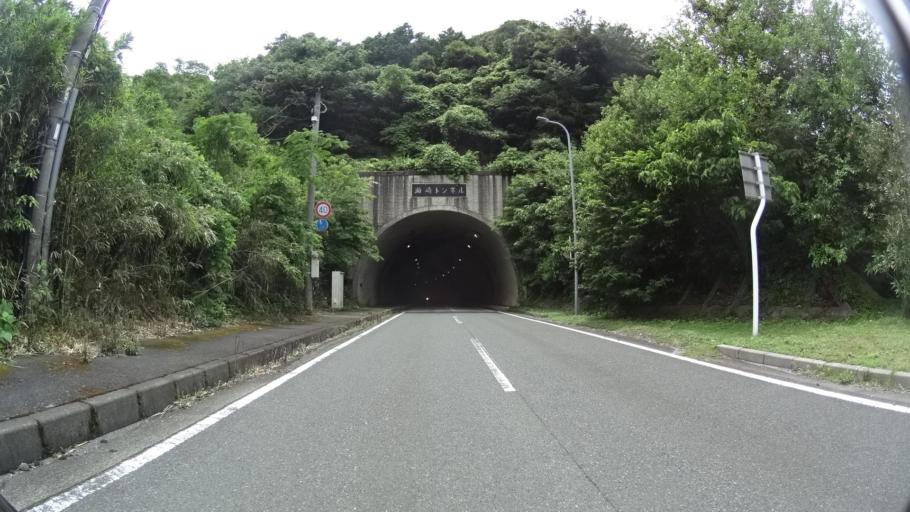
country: JP
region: Kyoto
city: Maizuru
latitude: 35.5359
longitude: 135.3480
